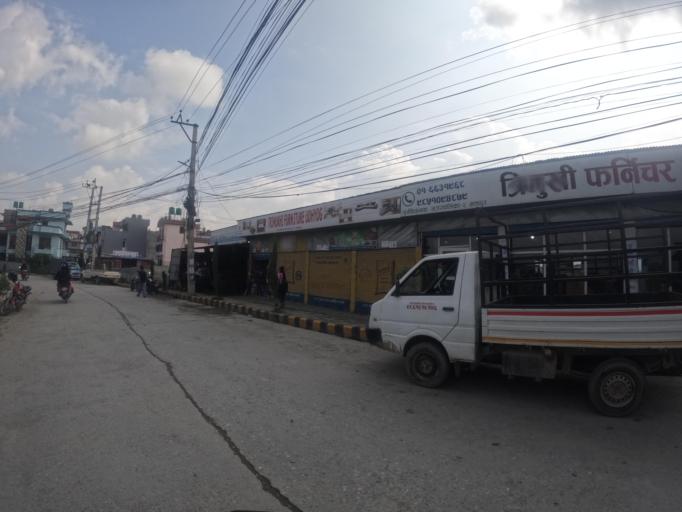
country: NP
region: Central Region
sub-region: Bagmati Zone
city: Patan
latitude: 27.6669
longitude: 85.3660
